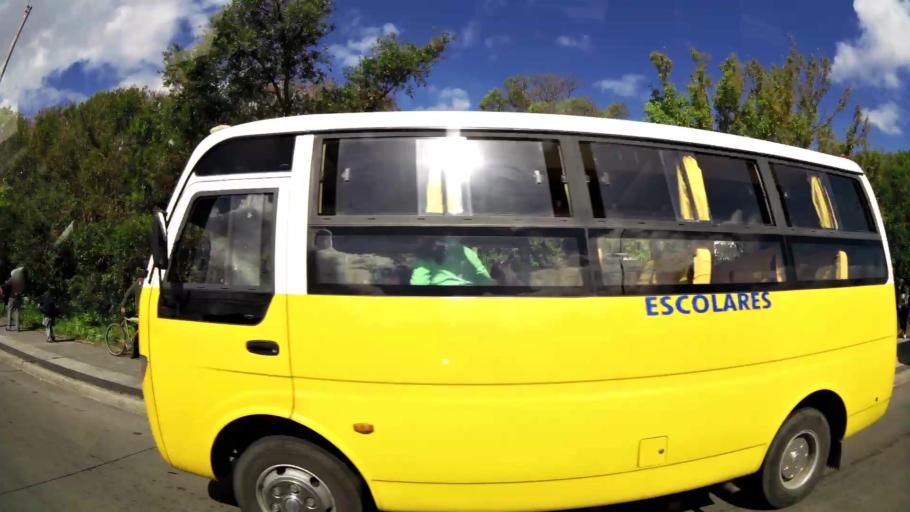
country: UY
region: Canelones
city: La Paz
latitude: -34.8338
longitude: -56.2214
